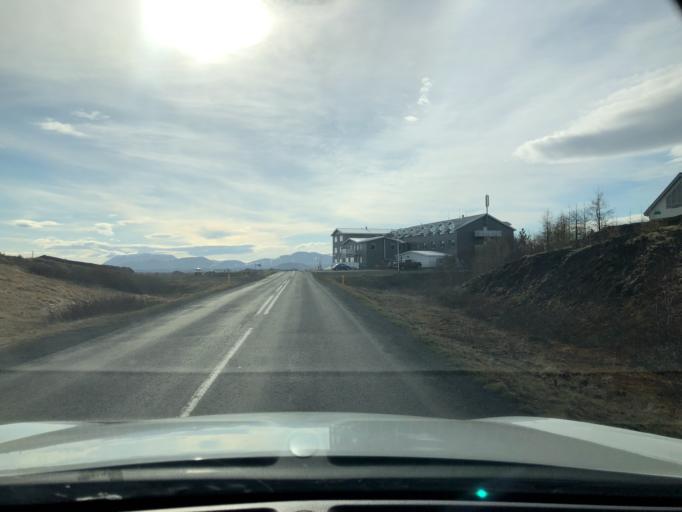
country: IS
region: Northeast
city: Laugar
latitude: 65.5679
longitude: -17.0400
